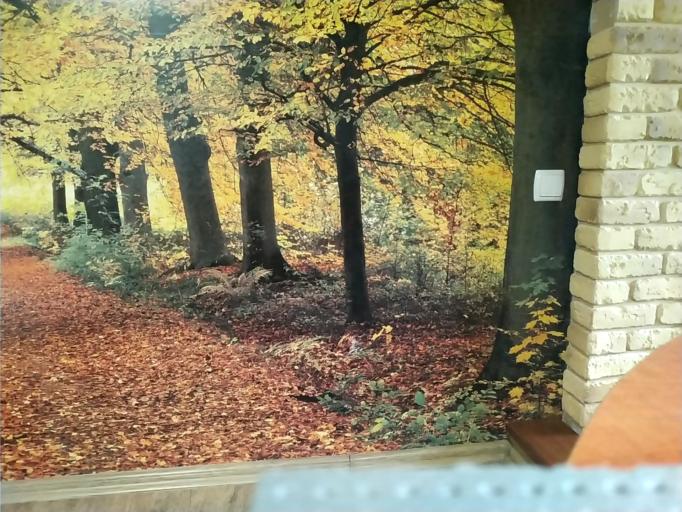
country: RU
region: Tverskaya
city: Staritsa
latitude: 56.5259
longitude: 35.0539
